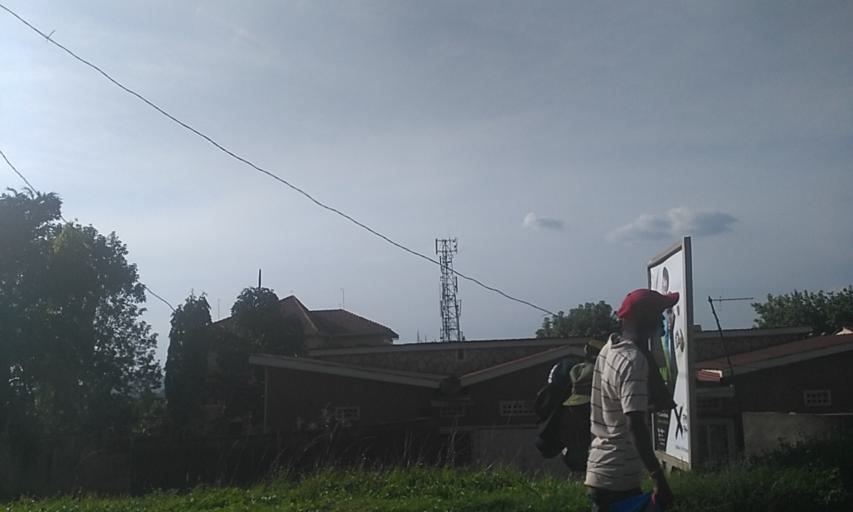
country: UG
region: Central Region
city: Kampala Central Division
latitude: 0.3204
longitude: 32.5581
